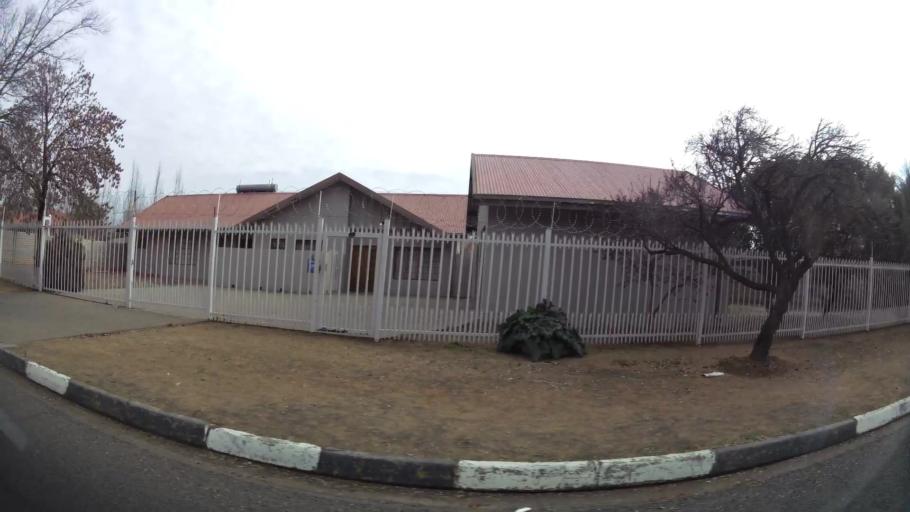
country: ZA
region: Orange Free State
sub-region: Mangaung Metropolitan Municipality
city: Bloemfontein
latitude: -29.1230
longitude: 26.1892
